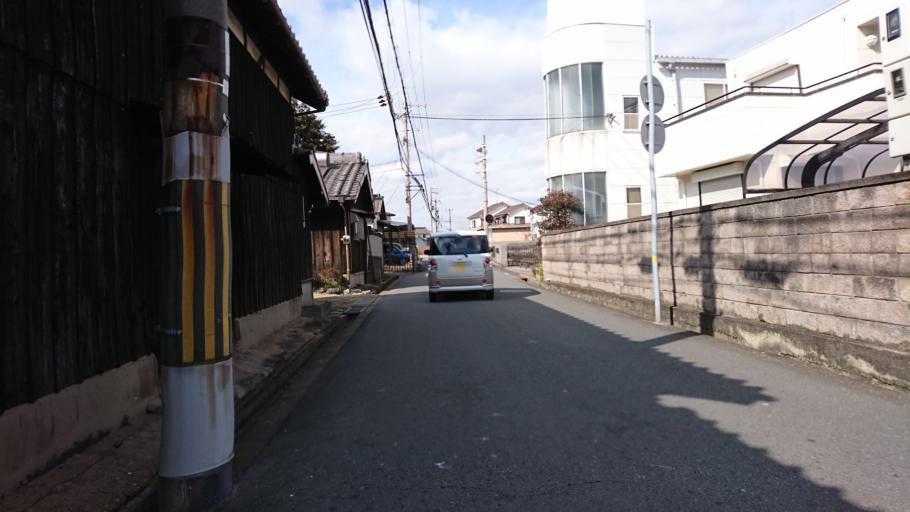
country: JP
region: Hyogo
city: Kakogawacho-honmachi
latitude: 34.7306
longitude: 134.8433
